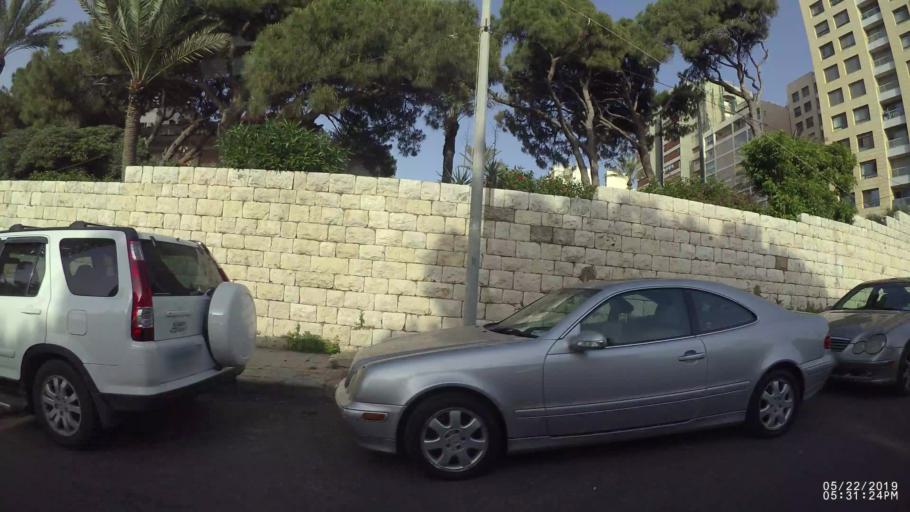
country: LB
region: Beyrouth
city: Ra's Bayrut
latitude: 33.8927
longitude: 35.4747
